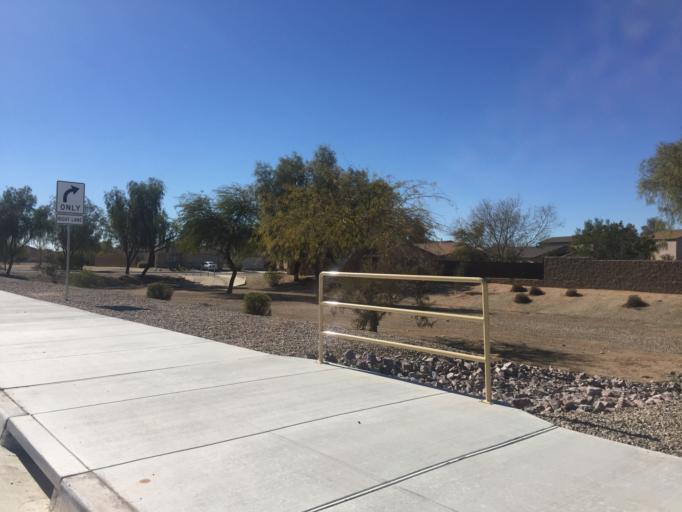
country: US
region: Arizona
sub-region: Pinal County
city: San Tan Valley
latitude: 33.1596
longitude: -111.5449
